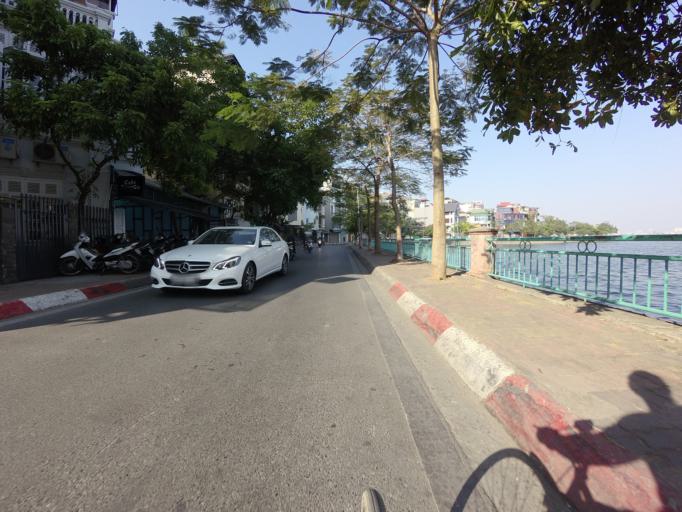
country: VN
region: Ha Noi
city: Dong Da
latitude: 21.0421
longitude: 105.8269
